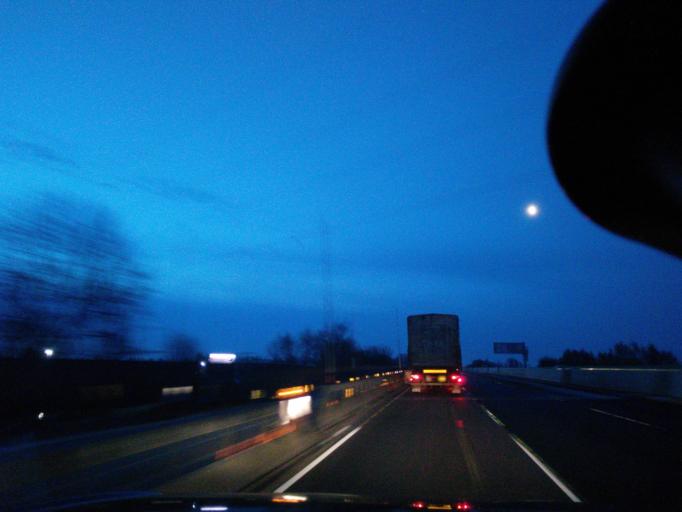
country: GB
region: England
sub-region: Derbyshire
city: Long Eaton
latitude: 52.8743
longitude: -1.3094
